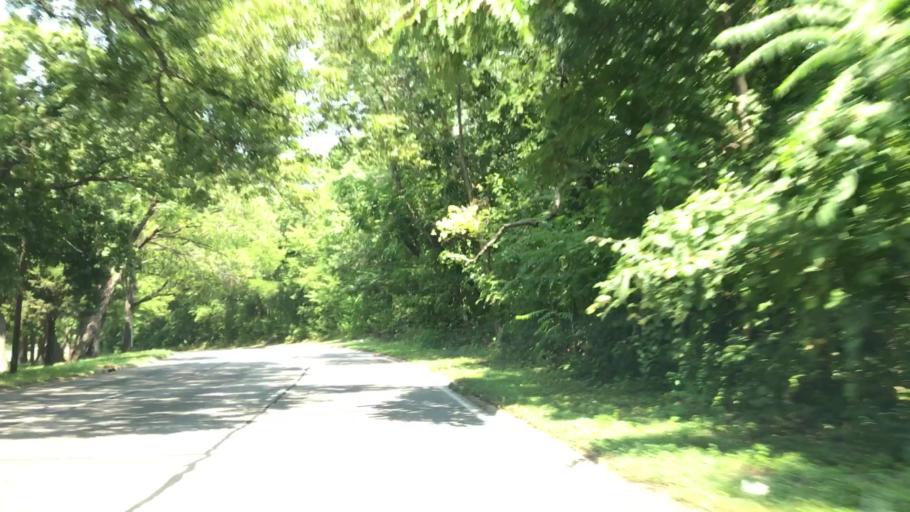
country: US
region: Texas
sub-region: Dallas County
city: Highland Park
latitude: 32.7998
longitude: -96.7385
